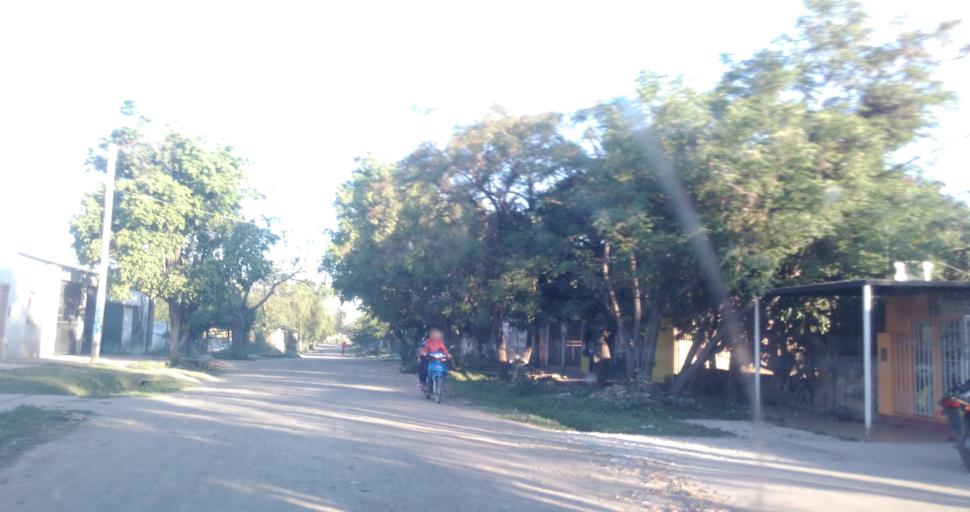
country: AR
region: Chaco
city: Fontana
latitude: -27.4261
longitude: -59.0221
